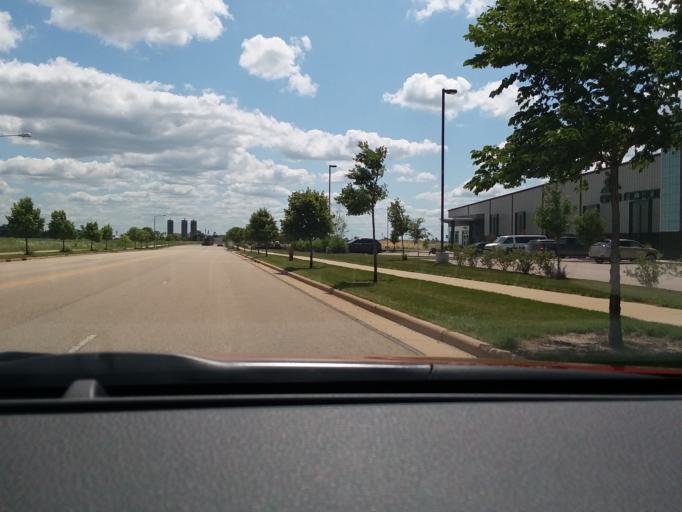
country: US
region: Wisconsin
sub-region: Dane County
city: Windsor
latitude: 43.1998
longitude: -89.3294
